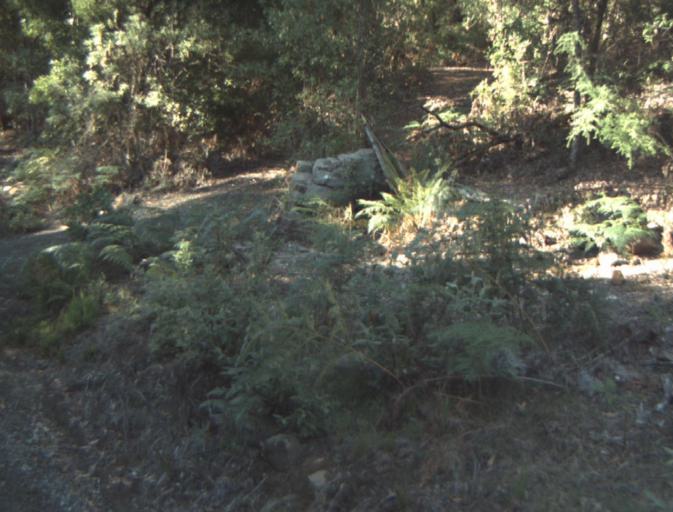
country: AU
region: Tasmania
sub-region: Launceston
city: Mayfield
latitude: -41.3011
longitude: 147.1899
